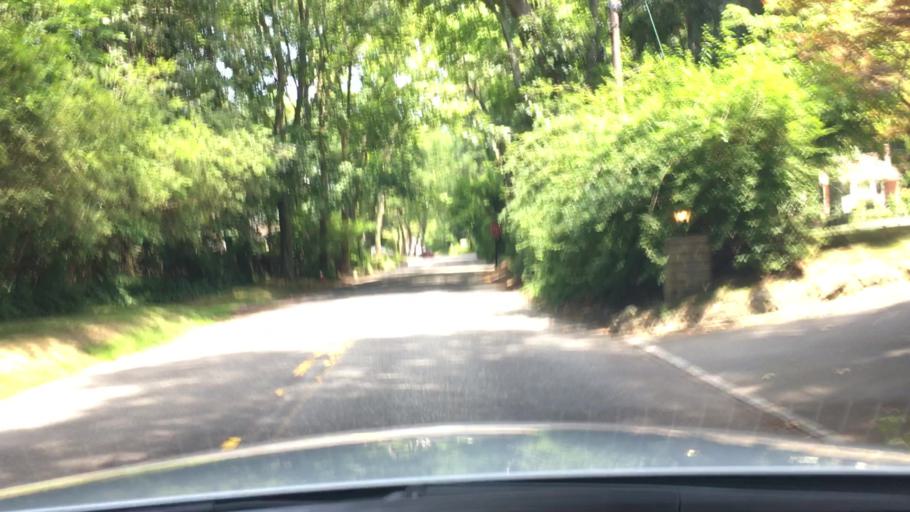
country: US
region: New York
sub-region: Suffolk County
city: West Hills
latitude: 40.8243
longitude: -73.4392
